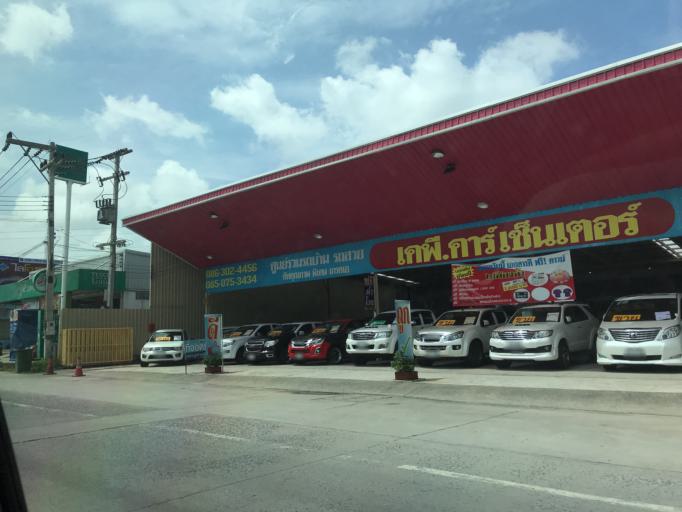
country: TH
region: Chon Buri
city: Si Racha
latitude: 13.1486
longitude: 100.9770
